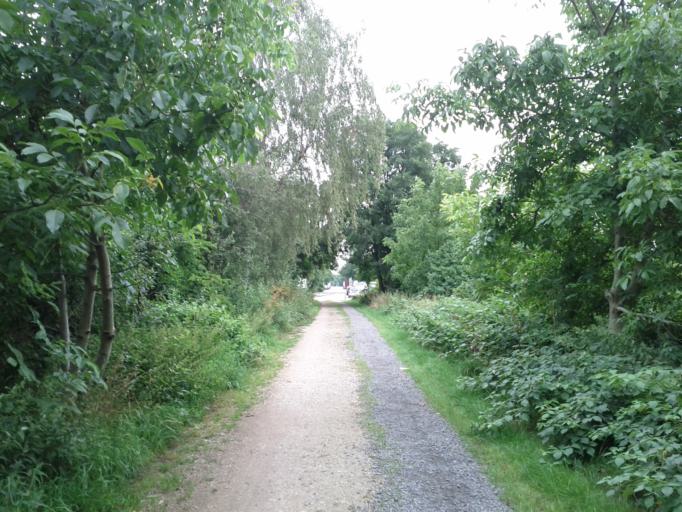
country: DE
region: Lower Saxony
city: Langenhagen
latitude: 52.4308
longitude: 9.6737
